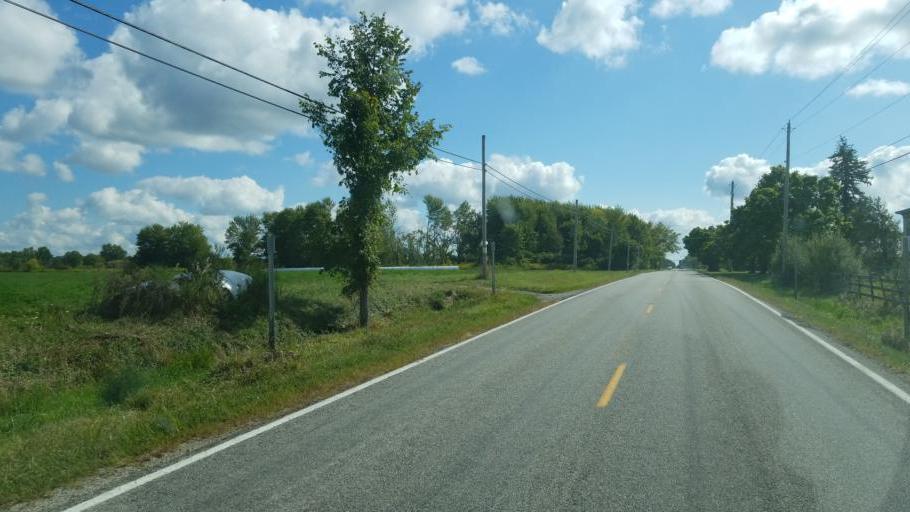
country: US
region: Ohio
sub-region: Lorain County
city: Lagrange
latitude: 41.2372
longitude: -82.1452
